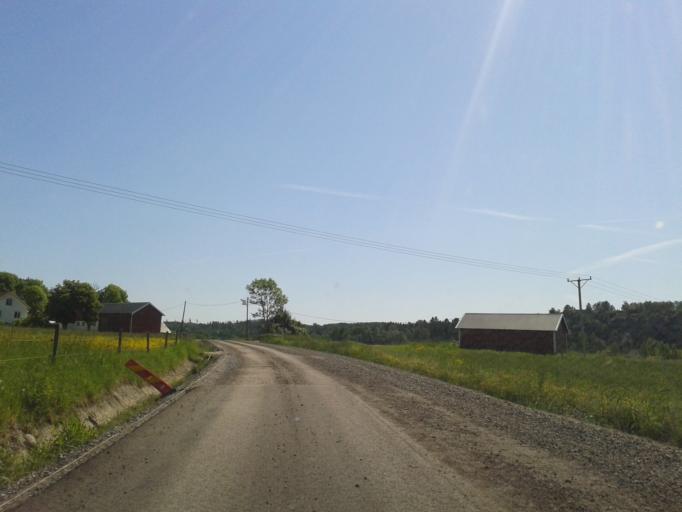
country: SE
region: Vaestra Goetaland
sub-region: Orust
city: Henan
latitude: 58.2574
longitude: 11.7380
